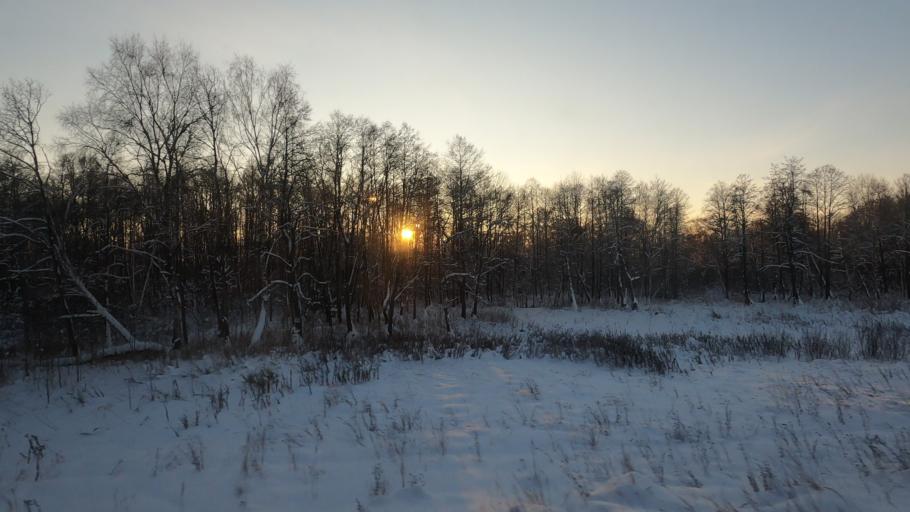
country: RU
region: Moskovskaya
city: Orud'yevo
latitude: 56.3939
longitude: 37.4998
